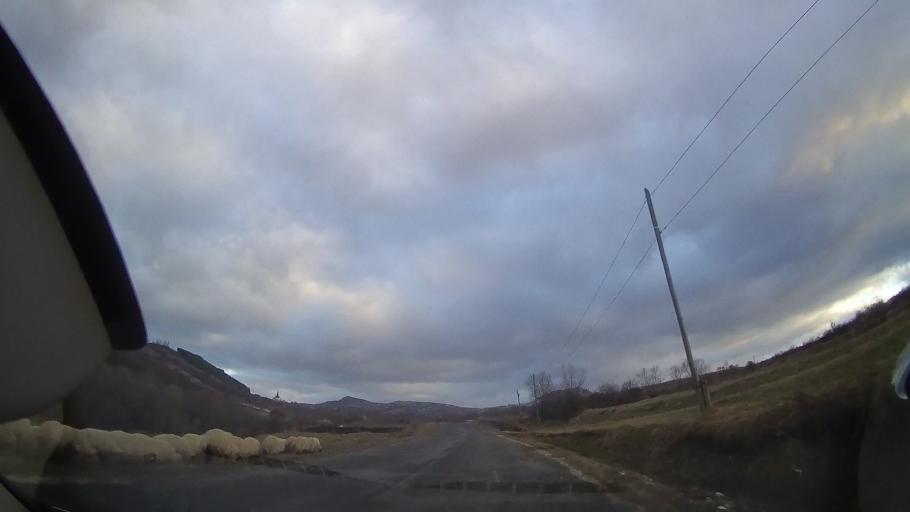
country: RO
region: Cluj
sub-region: Comuna Calatele
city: Calatele
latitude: 46.7852
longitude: 23.0158
